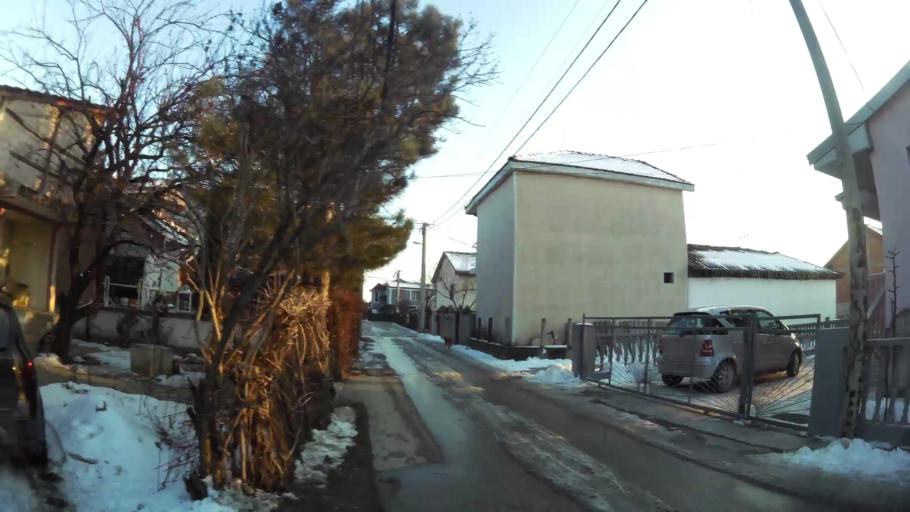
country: MK
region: Kisela Voda
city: Kisela Voda
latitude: 41.9779
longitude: 21.4937
